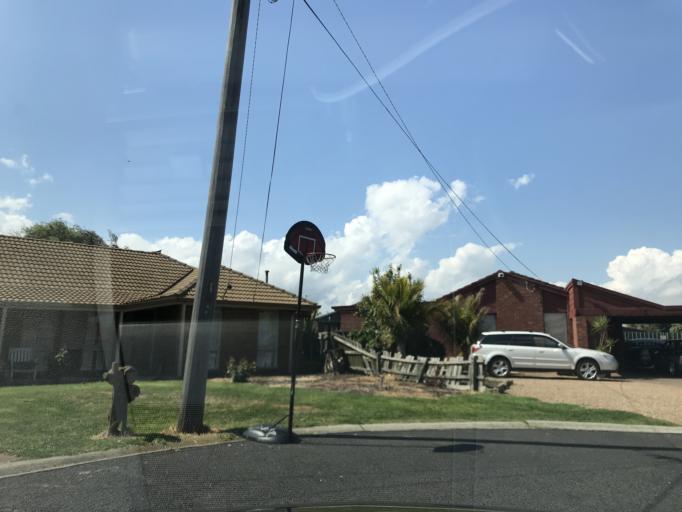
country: AU
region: Victoria
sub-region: Wyndham
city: Hoppers Crossing
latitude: -37.8684
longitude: 144.7053
